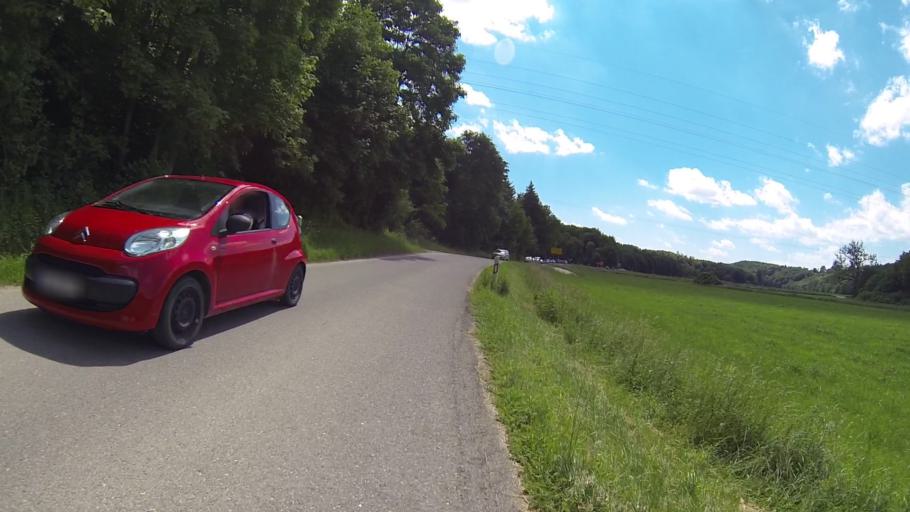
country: DE
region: Baden-Wuerttemberg
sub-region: Tuebingen Region
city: Asselfingen
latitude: 48.5613
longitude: 10.1951
